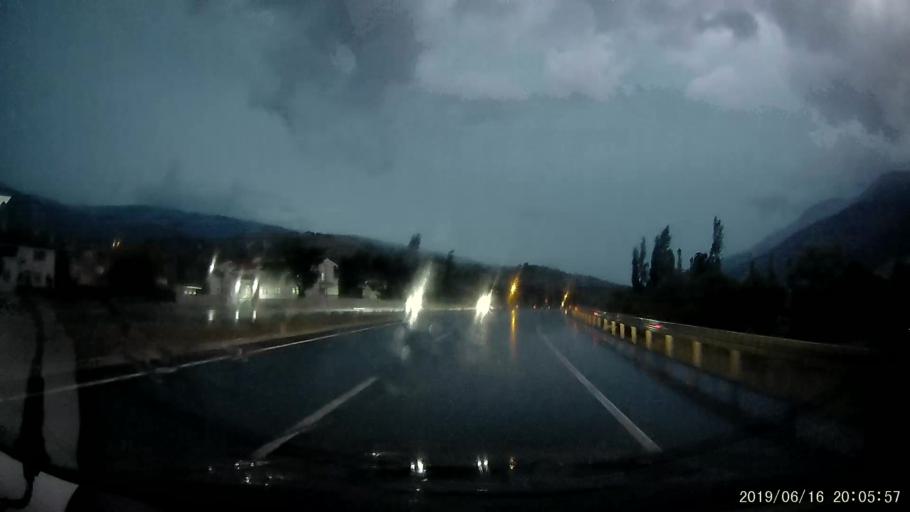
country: TR
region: Sivas
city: Dogansar
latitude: 40.3120
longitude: 37.6475
